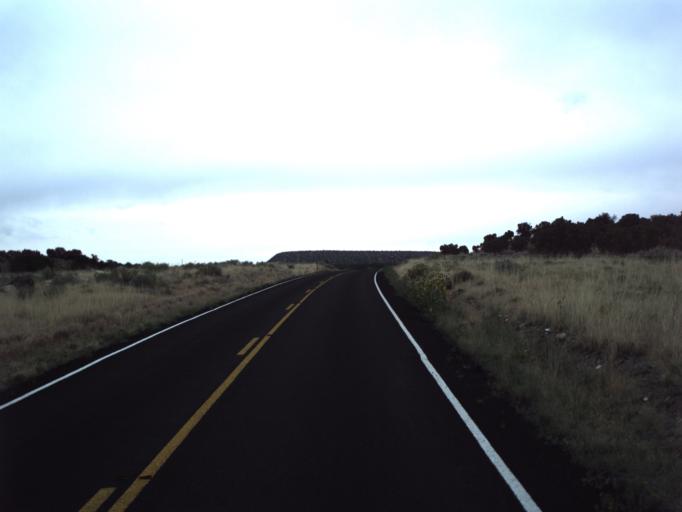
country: US
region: Utah
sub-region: Carbon County
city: East Carbon City
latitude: 39.4763
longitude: -110.3985
